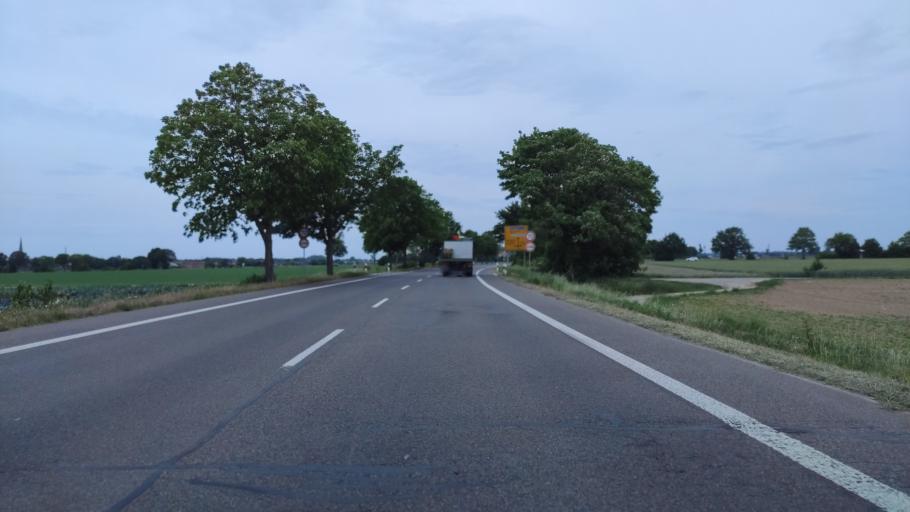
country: DE
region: North Rhine-Westphalia
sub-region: Regierungsbezirk Dusseldorf
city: Kaarst
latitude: 51.1880
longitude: 6.5758
